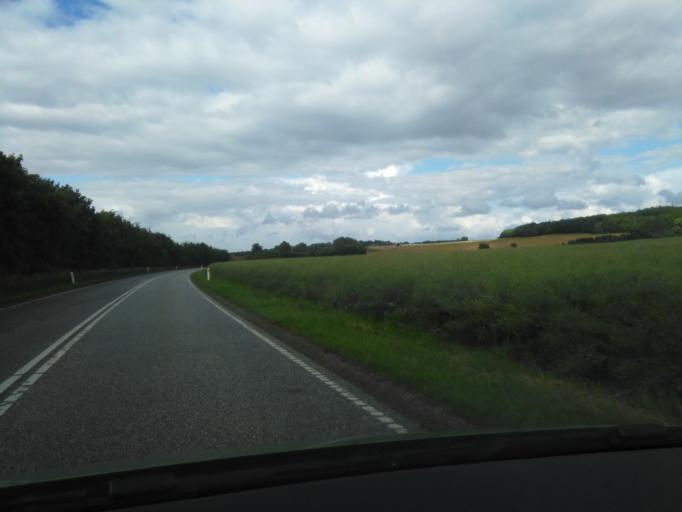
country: DK
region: Central Jutland
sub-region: Skanderborg Kommune
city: Ry
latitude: 56.0042
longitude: 9.7740
